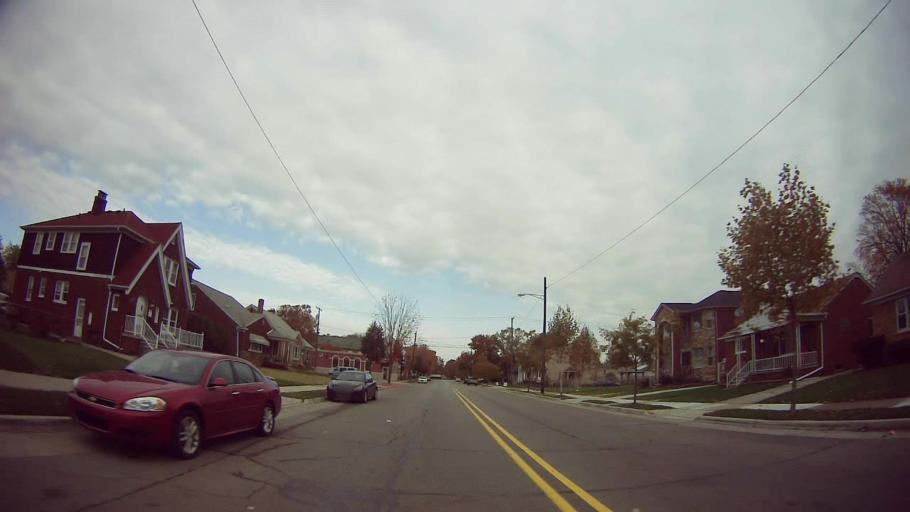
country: US
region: Michigan
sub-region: Wayne County
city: Dearborn
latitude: 42.3487
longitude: -83.1868
